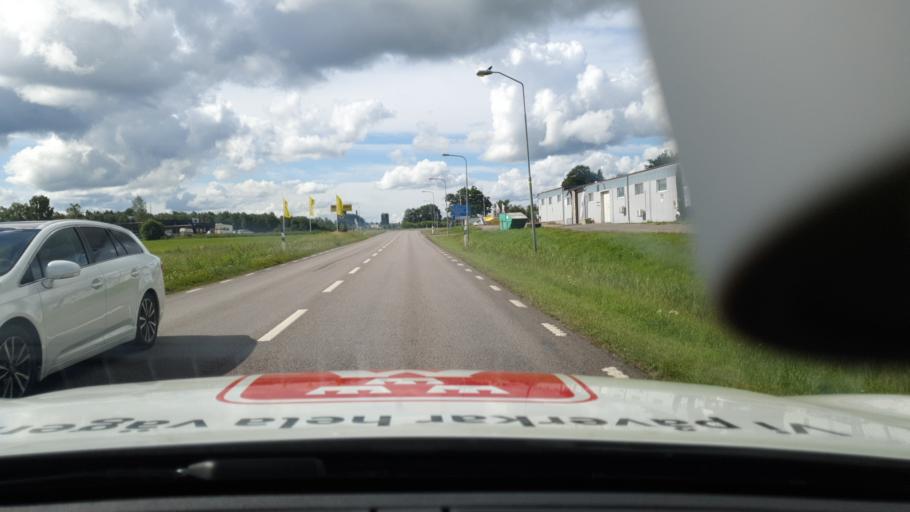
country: SE
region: Vaestra Goetaland
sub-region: Falkopings Kommun
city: Falkoeping
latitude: 58.0887
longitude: 13.5237
